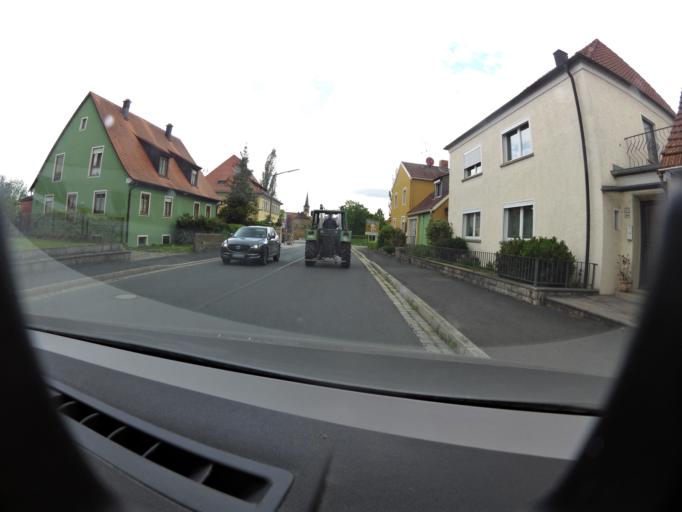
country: DE
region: Bavaria
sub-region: Regierungsbezirk Unterfranken
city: Iphofen
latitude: 49.7001
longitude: 10.2600
